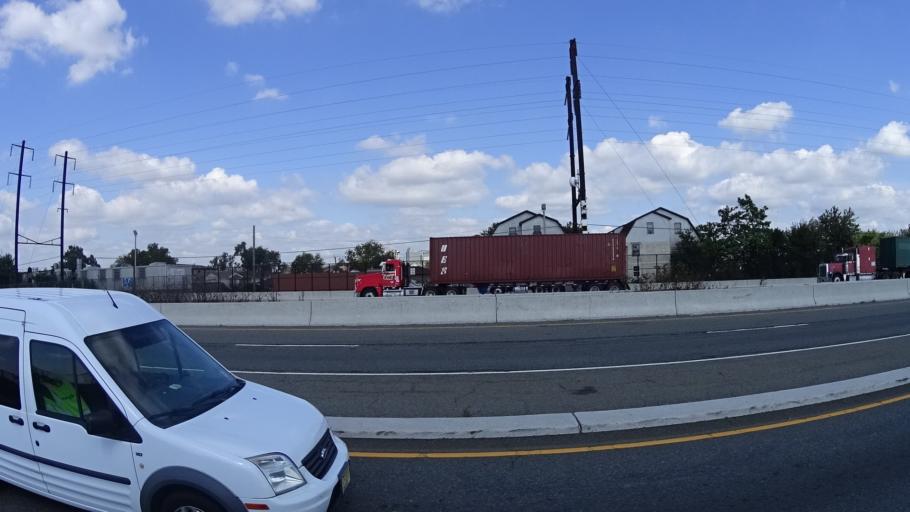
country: US
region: New Jersey
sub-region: Hudson County
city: Harrison
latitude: 40.7224
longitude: -74.1465
